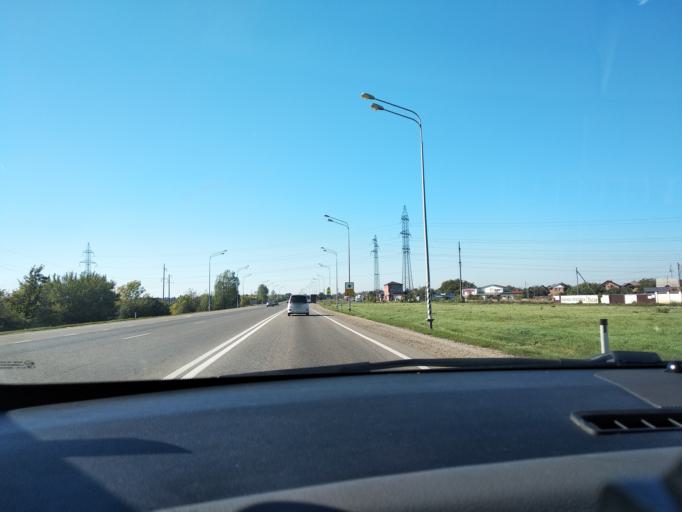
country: RU
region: Krasnodarskiy
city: Agronom
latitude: 45.1602
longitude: 39.0788
